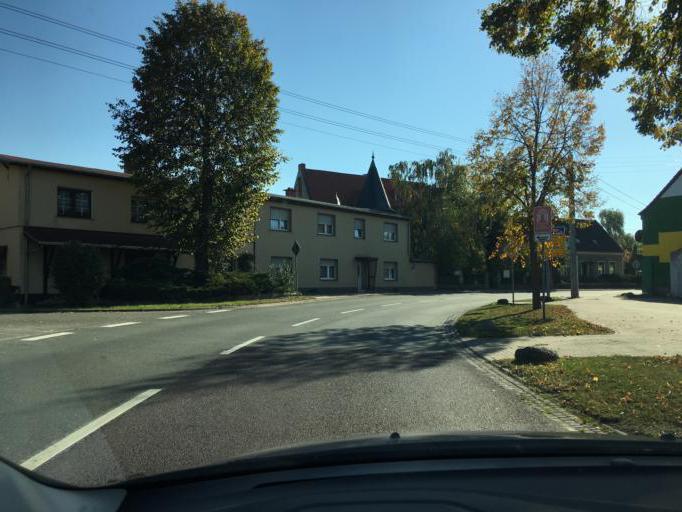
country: DE
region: Saxony-Anhalt
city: Brumby
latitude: 51.8524
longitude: 11.7086
